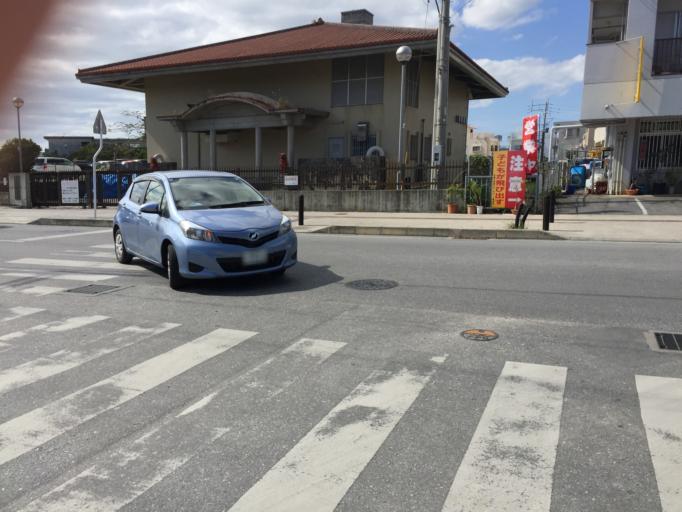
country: JP
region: Okinawa
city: Ginowan
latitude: 26.2315
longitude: 127.7335
